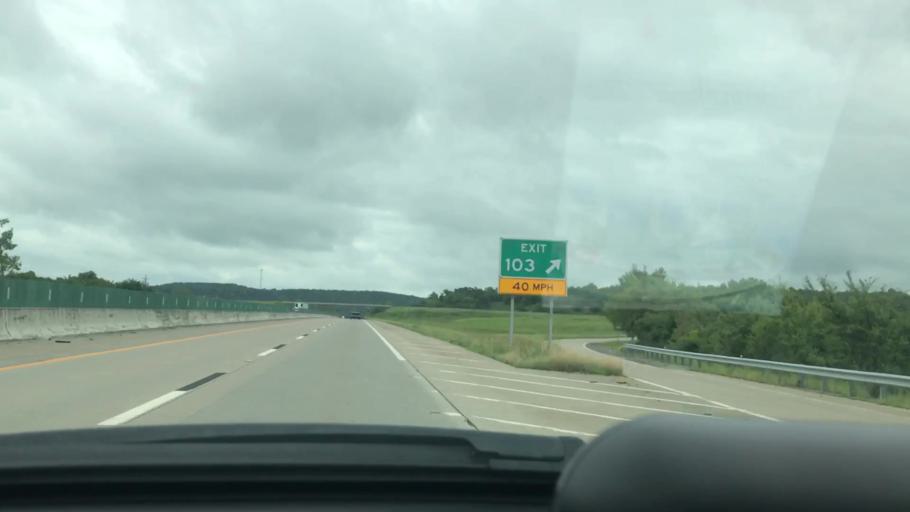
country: US
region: Oklahoma
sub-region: Pittsburg County
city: Krebs
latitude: 35.0982
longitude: -95.6978
